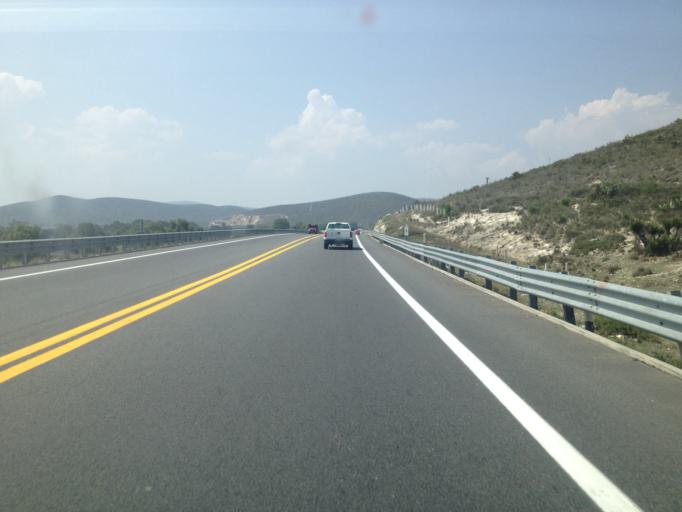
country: MX
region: Puebla
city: Cuacnopalan
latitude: 18.8177
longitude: -97.4912
